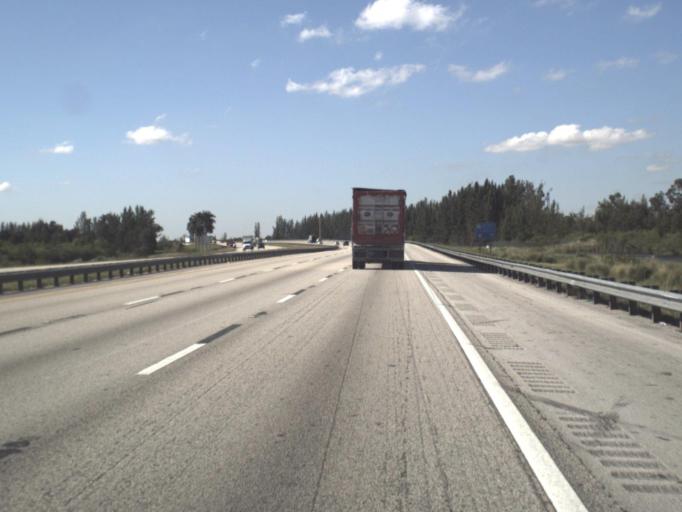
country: US
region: Florida
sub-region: Miami-Dade County
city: Palm Springs North
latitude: 25.9324
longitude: -80.3714
